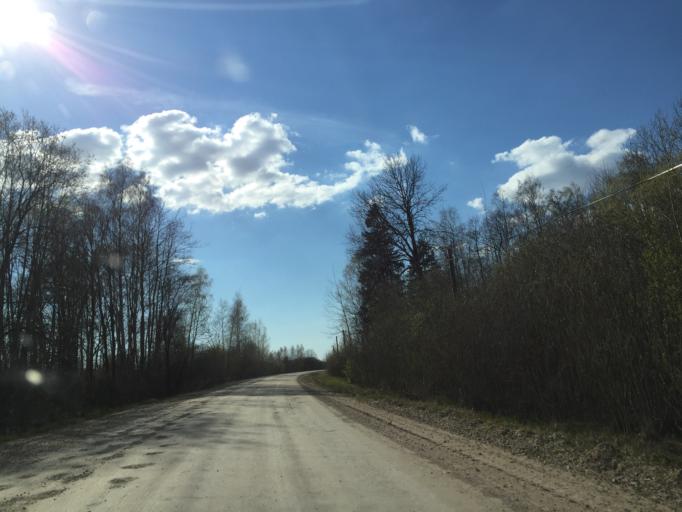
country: LV
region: Saulkrastu
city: Saulkrasti
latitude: 57.3457
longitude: 24.5863
